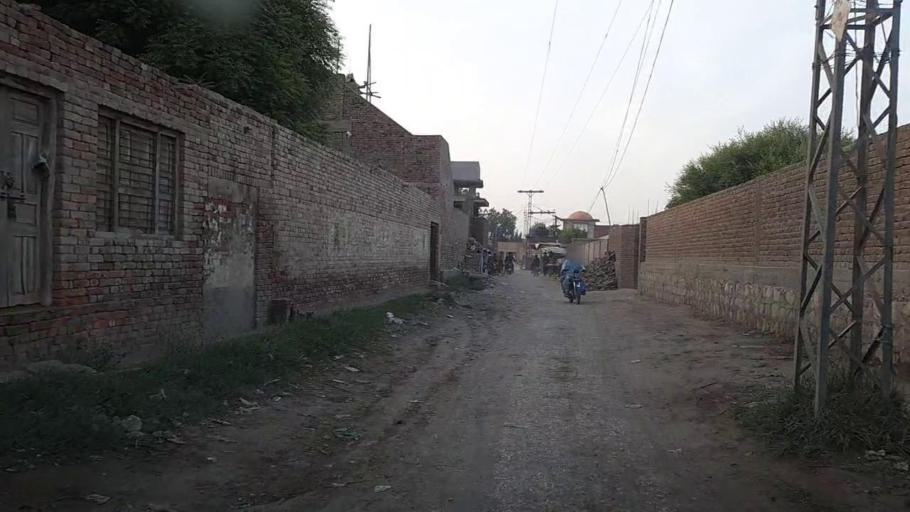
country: PK
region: Sindh
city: Ubauro
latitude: 28.2962
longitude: 69.7993
